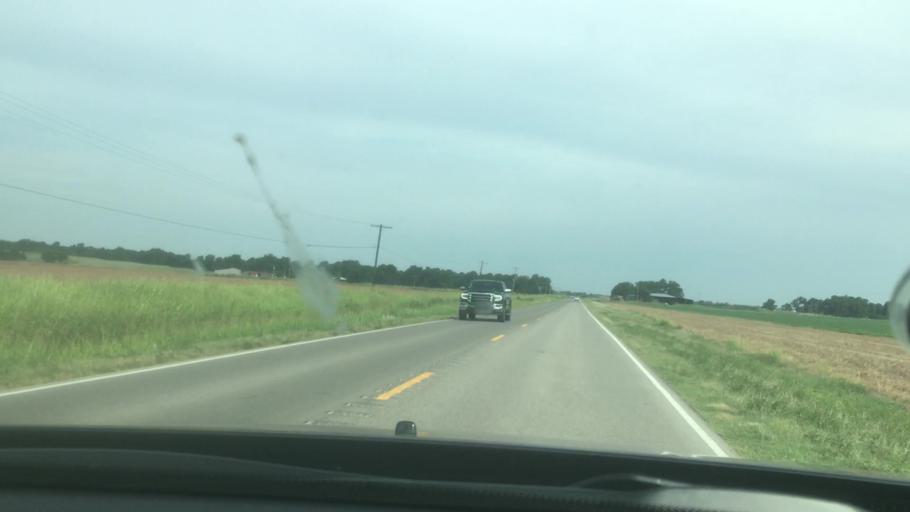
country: US
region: Oklahoma
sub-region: Garvin County
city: Maysville
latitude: 34.7859
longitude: -97.3368
